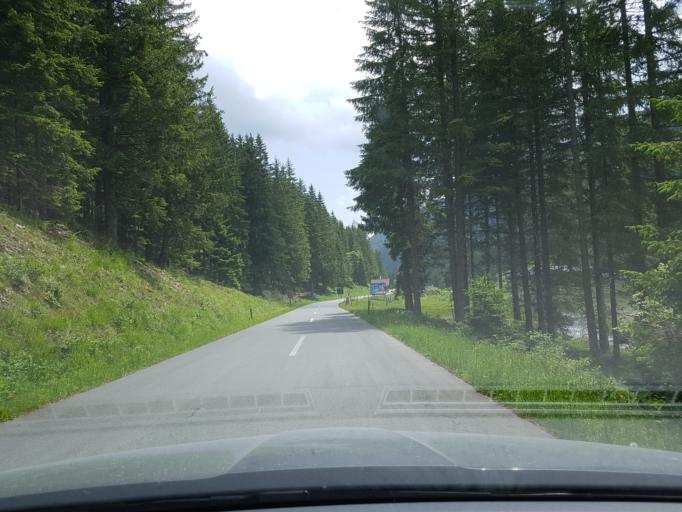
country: AT
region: Carinthia
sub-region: Politischer Bezirk Spittal an der Drau
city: Kleinkirchheim
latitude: 46.8858
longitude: 13.8485
